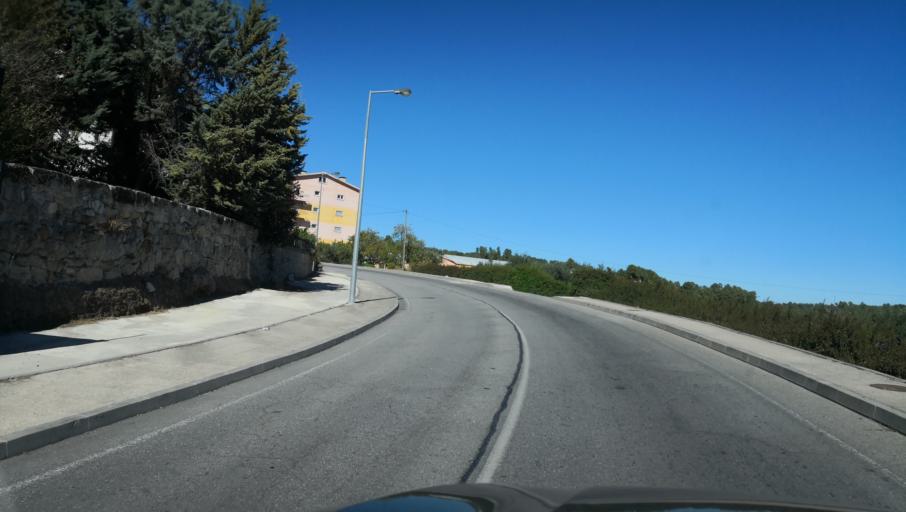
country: PT
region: Vila Real
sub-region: Valpacos
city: Valpacos
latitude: 41.6149
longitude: -7.3101
